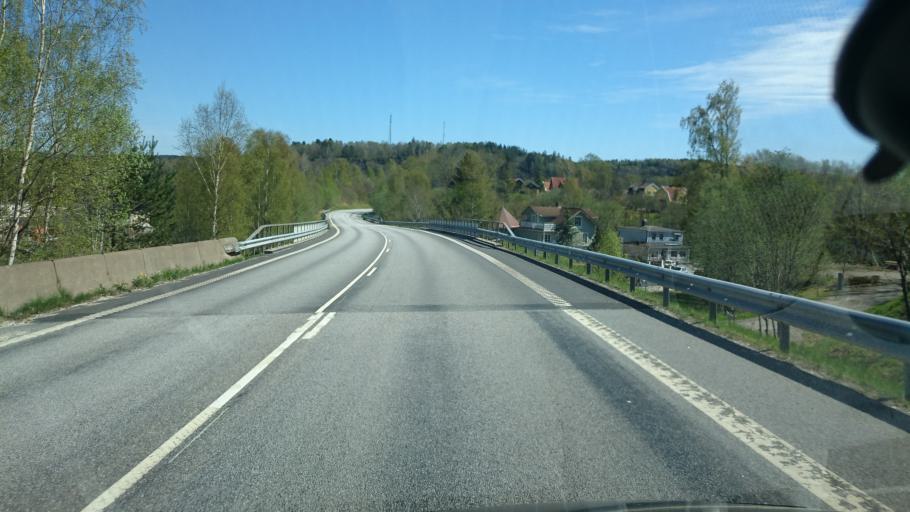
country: SE
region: Vaestra Goetaland
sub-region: Munkedals Kommun
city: Munkedal
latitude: 58.4694
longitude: 11.6700
